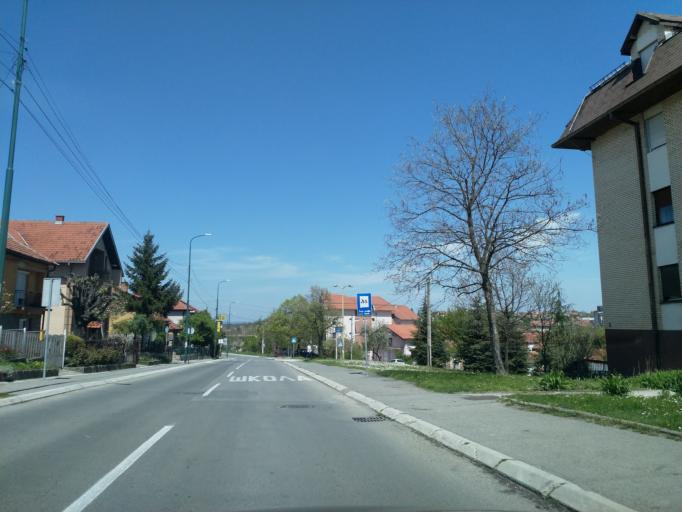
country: RS
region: Central Serbia
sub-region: Belgrade
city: Lazarevac
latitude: 44.3827
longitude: 20.2503
